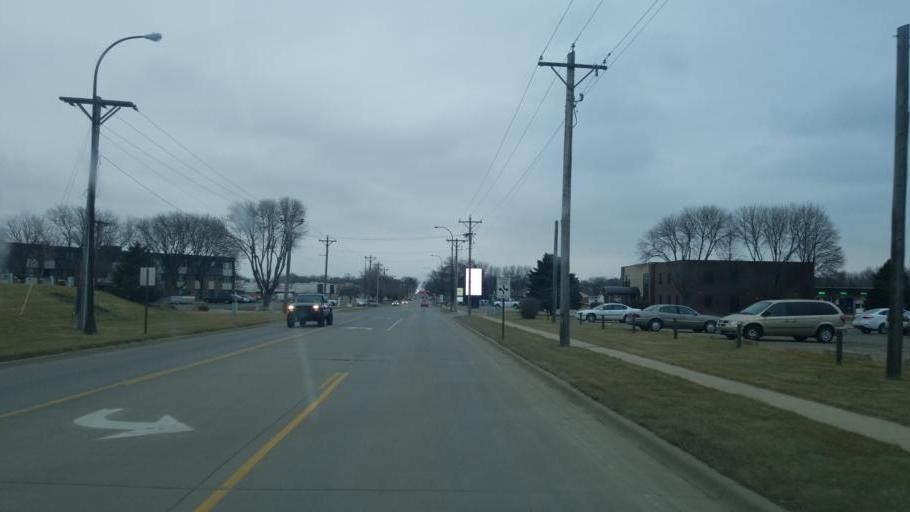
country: US
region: South Dakota
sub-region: Yankton County
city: Yankton
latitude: 42.8907
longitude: -97.4034
